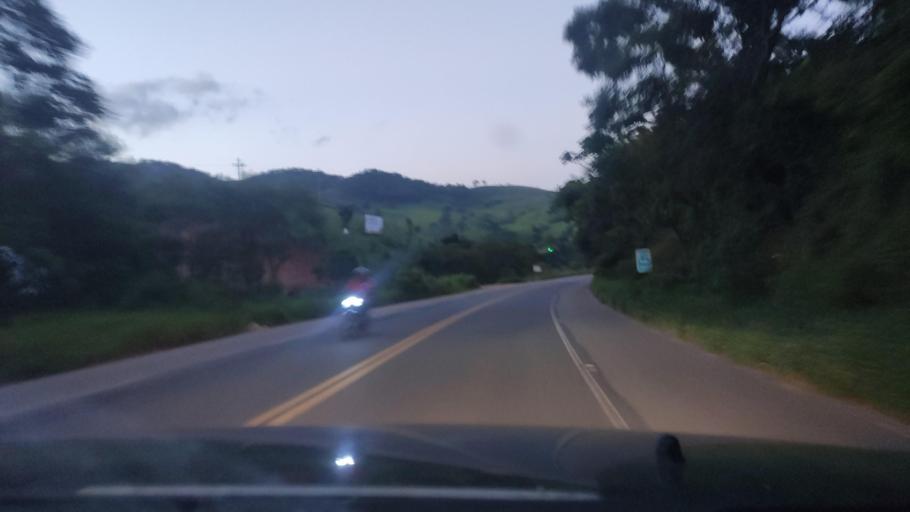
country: BR
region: Sao Paulo
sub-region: Campos Do Jordao
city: Campos do Jordao
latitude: -22.7352
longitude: -45.7425
